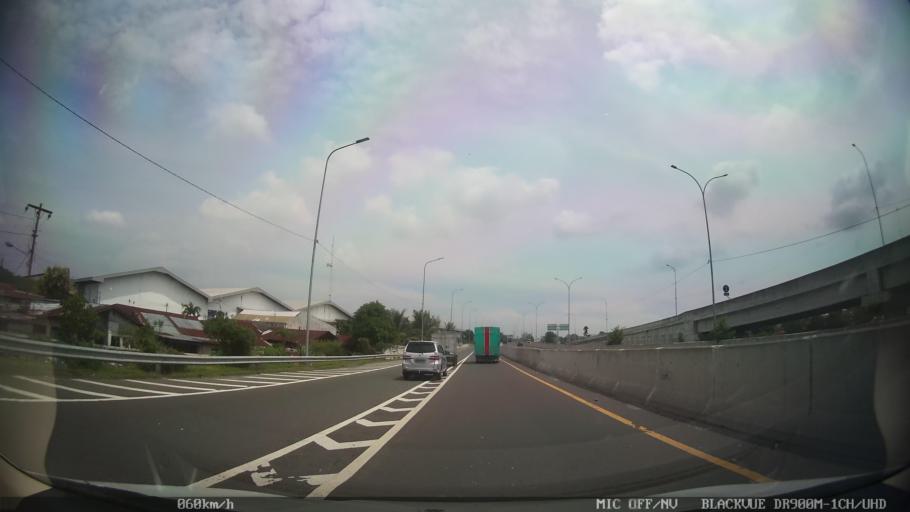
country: ID
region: North Sumatra
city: Medan
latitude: 3.6516
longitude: 98.6819
